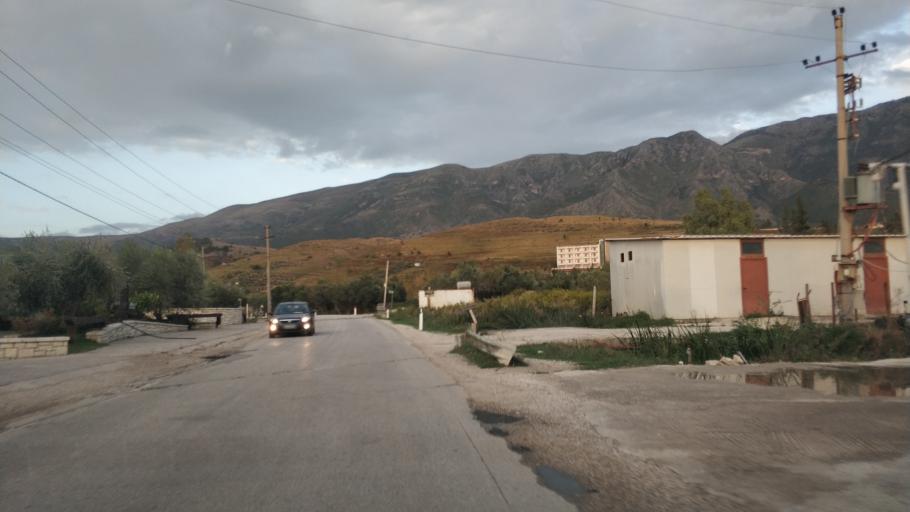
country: AL
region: Vlore
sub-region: Rrethi i Vlores
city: Orikum
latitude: 40.3450
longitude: 19.4838
